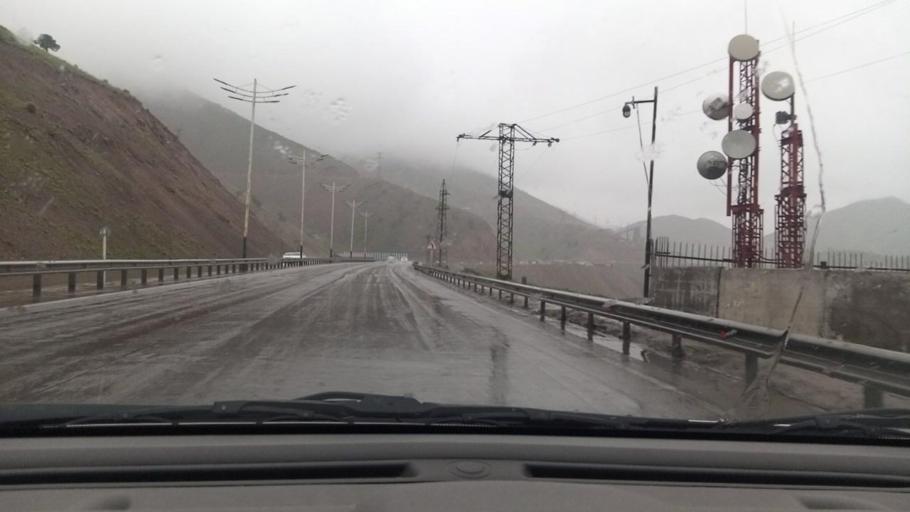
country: UZ
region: Toshkent
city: Angren
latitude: 41.0947
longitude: 70.5240
